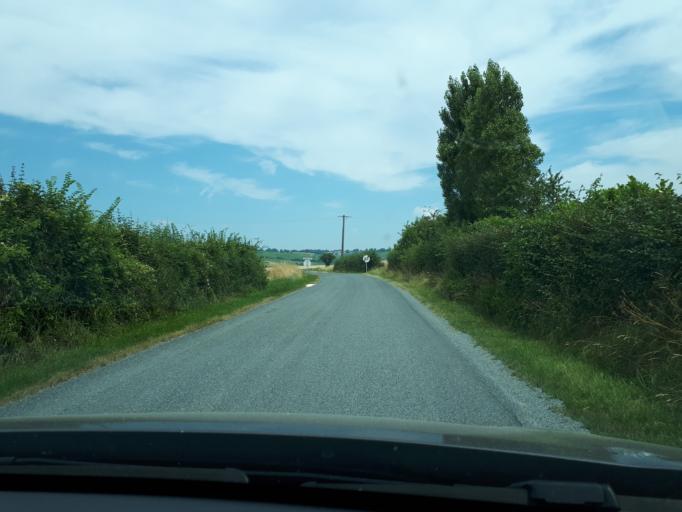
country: FR
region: Centre
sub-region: Departement du Cher
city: Sancerre
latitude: 47.2882
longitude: 2.7551
